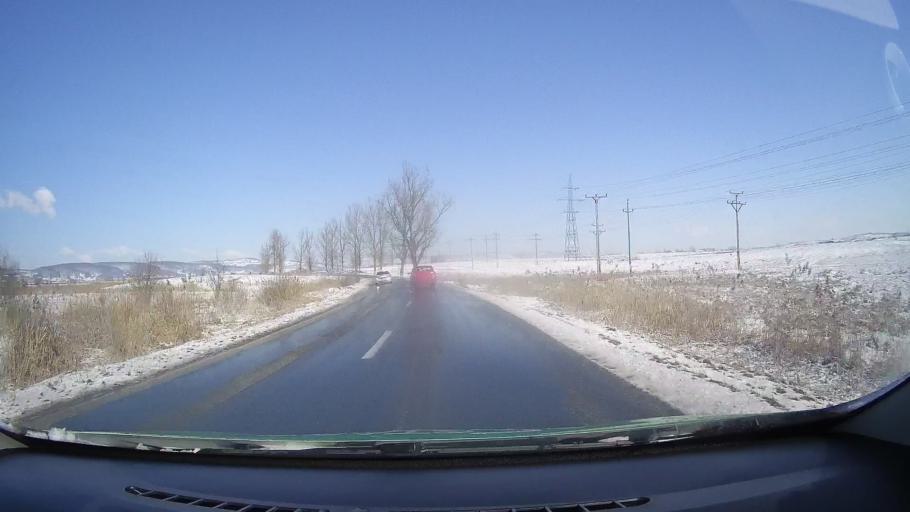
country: RO
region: Sibiu
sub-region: Comuna Avrig
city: Marsa
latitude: 45.7071
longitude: 24.3691
